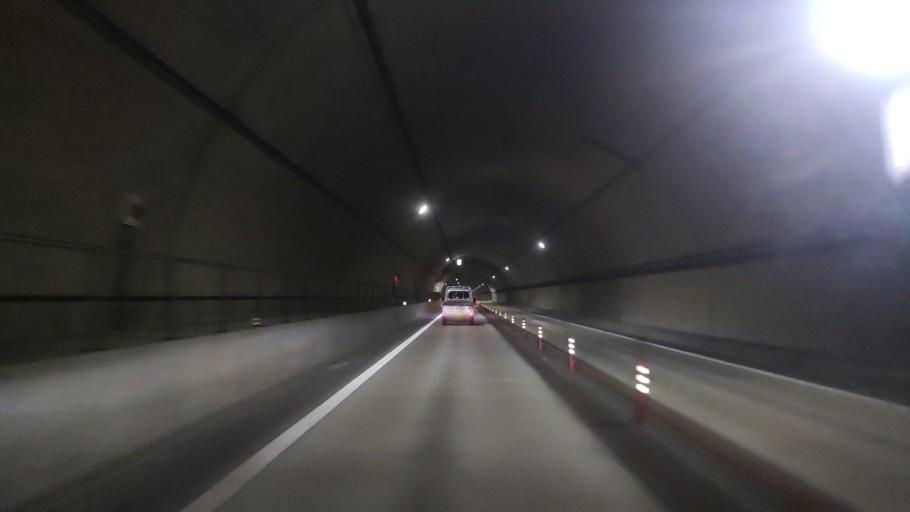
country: JP
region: Wakayama
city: Tanabe
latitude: 33.6212
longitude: 135.4198
